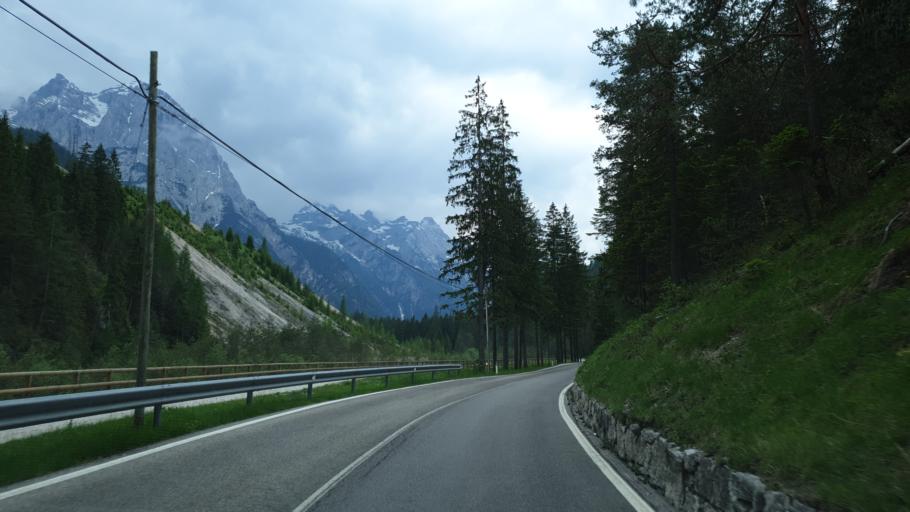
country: IT
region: Veneto
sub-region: Provincia di Belluno
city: Auronzo
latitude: 46.5658
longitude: 12.3498
